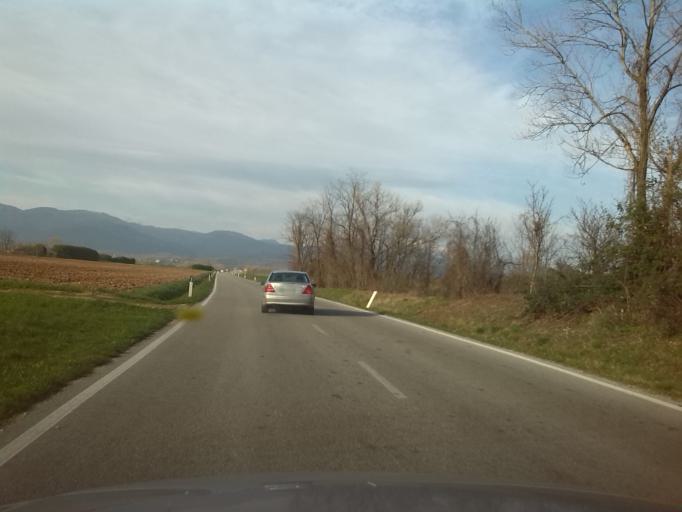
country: IT
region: Friuli Venezia Giulia
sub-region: Provincia di Udine
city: Premariacco
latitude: 46.0627
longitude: 13.4175
